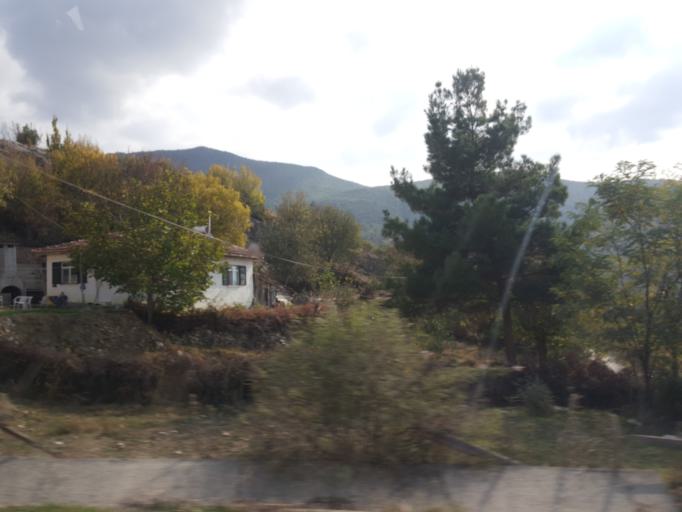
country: TR
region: Sinop
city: Sarayduzu
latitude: 41.3691
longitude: 34.8915
